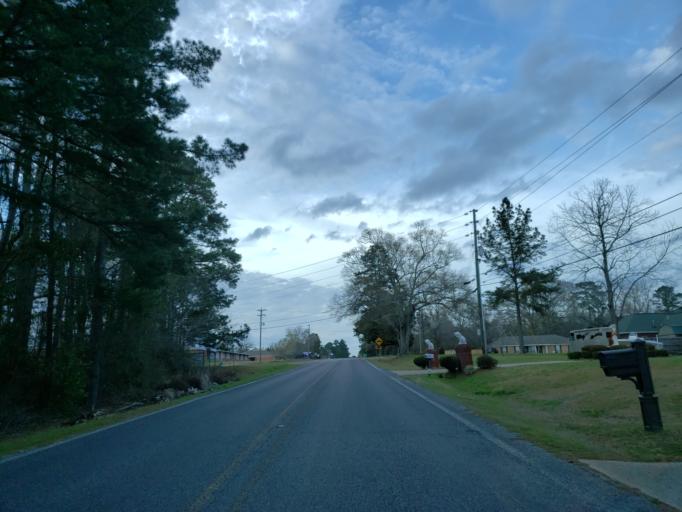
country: US
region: Mississippi
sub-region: Clarke County
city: Stonewall
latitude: 32.2237
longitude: -88.7002
